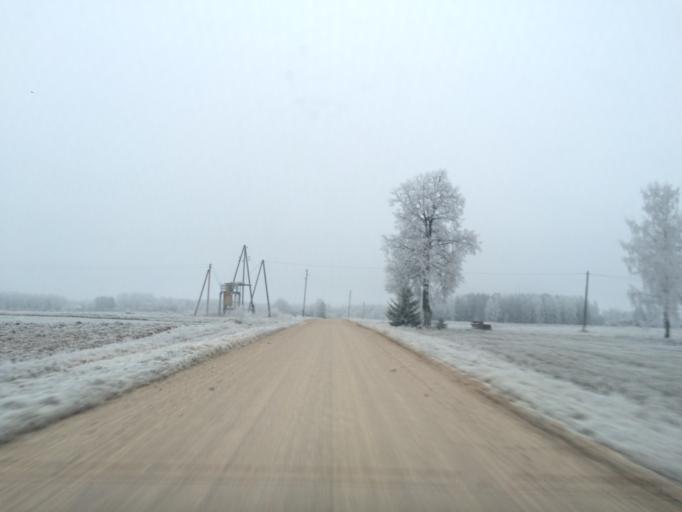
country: LV
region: Ludzas Rajons
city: Ludza
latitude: 56.6045
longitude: 27.5171
